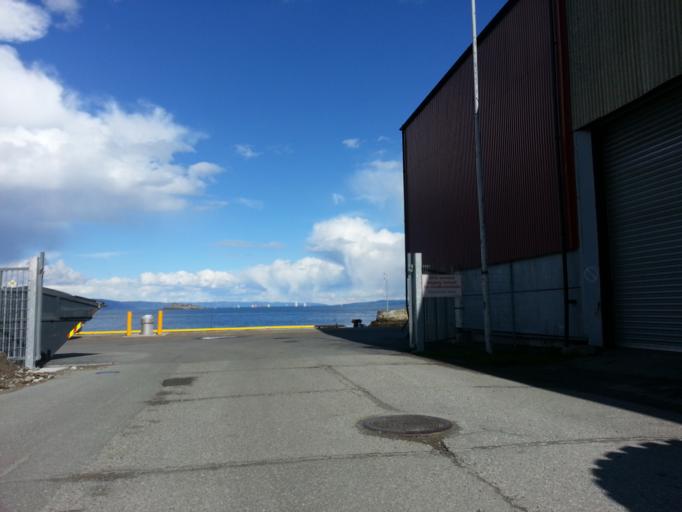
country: NO
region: Sor-Trondelag
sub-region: Trondheim
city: Trondheim
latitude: 63.4331
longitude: 10.3646
